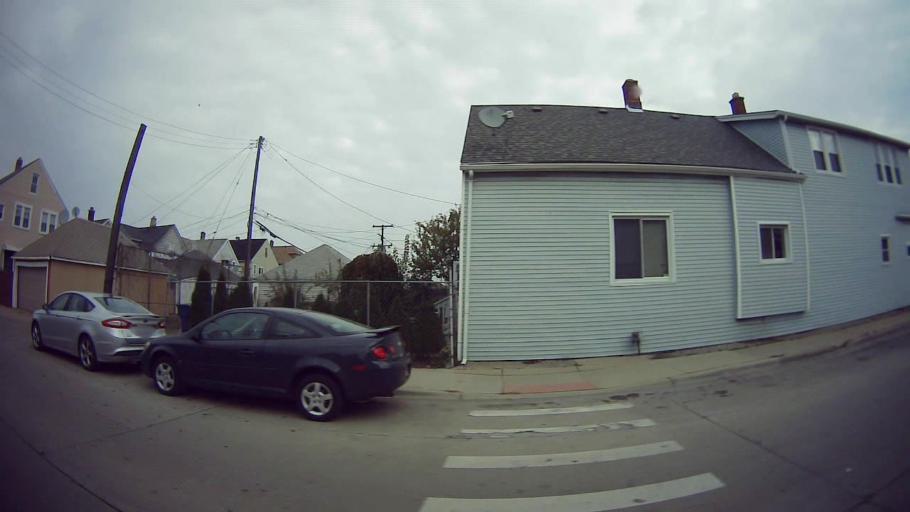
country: US
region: Michigan
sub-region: Wayne County
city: Hamtramck
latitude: 42.4010
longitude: -83.0638
